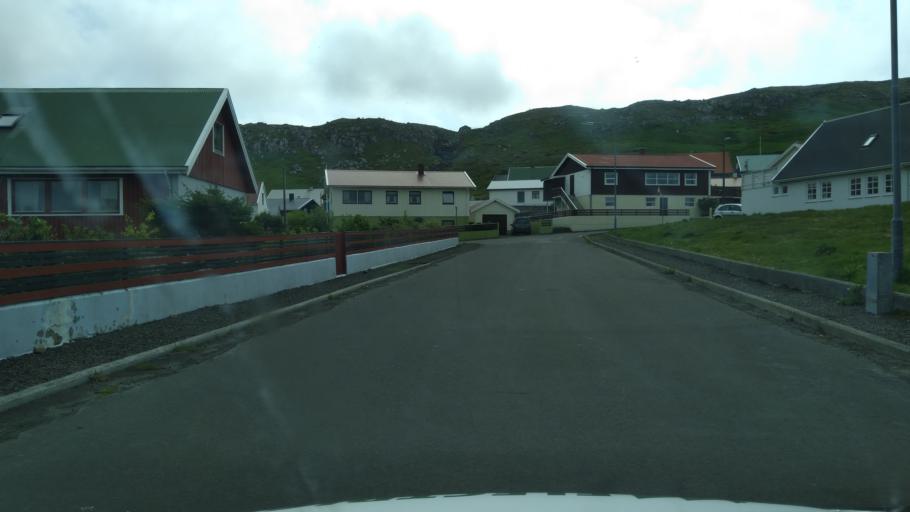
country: FO
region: Sandoy
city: Sandur
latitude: 61.9036
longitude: -6.8886
